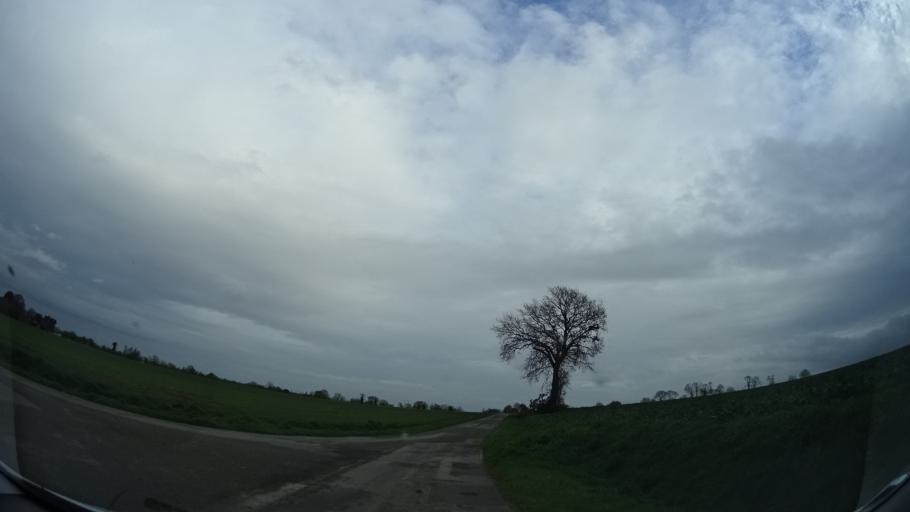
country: FR
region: Brittany
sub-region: Departement des Cotes-d'Armor
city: Evran
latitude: 48.3359
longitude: -1.9603
